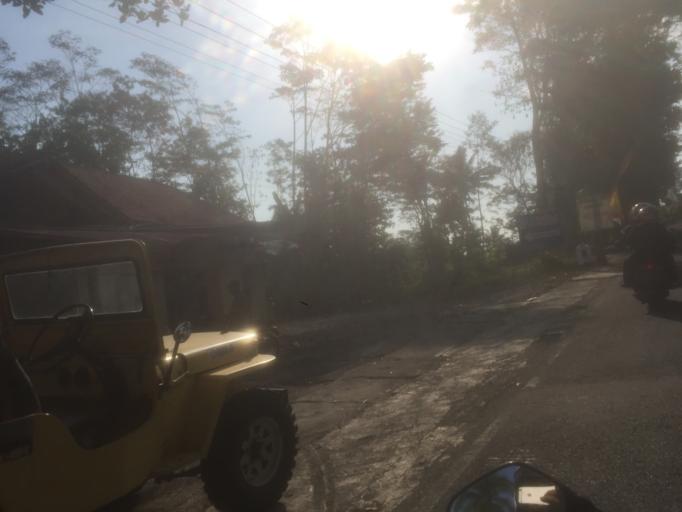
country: ID
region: Daerah Istimewa Yogyakarta
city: Sleman
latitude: -7.6552
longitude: 110.4237
